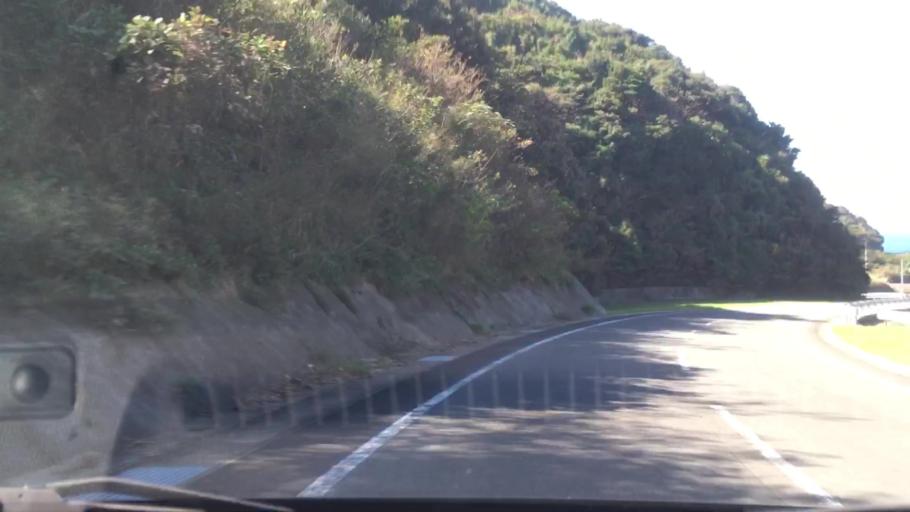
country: JP
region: Nagasaki
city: Sasebo
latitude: 33.0073
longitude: 129.5653
